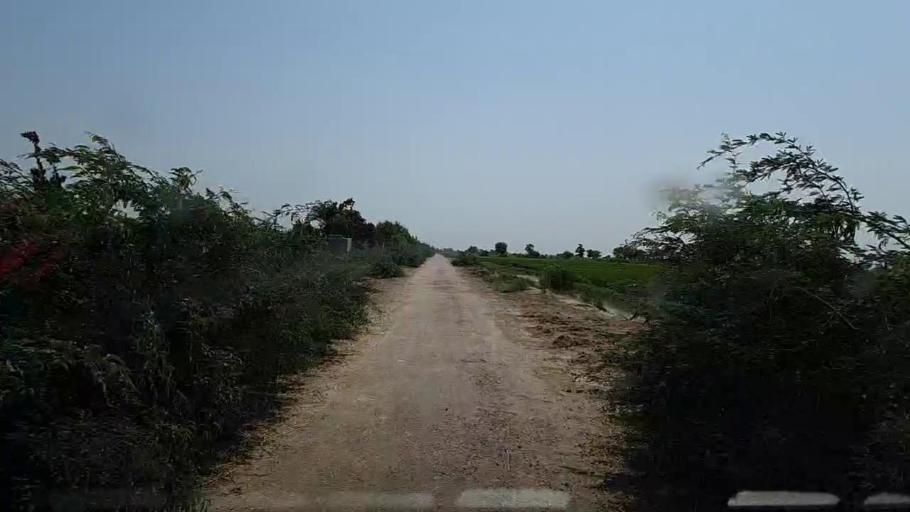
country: PK
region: Sindh
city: Mirpur Batoro
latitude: 24.6136
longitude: 68.4523
